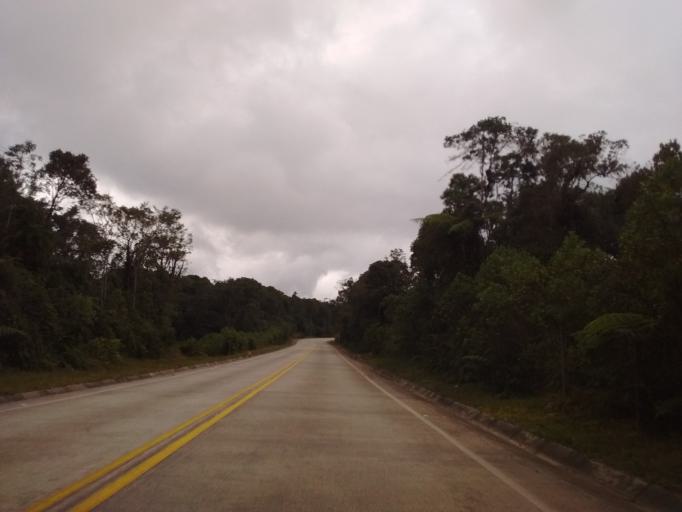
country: CO
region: Huila
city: Isnos
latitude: 2.0462
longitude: -76.3009
